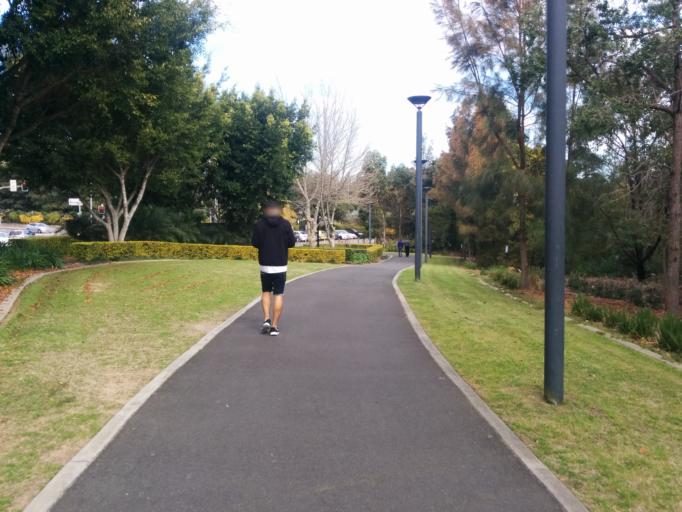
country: AU
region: New South Wales
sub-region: Canada Bay
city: Rhodes
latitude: -33.8358
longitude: 151.0836
